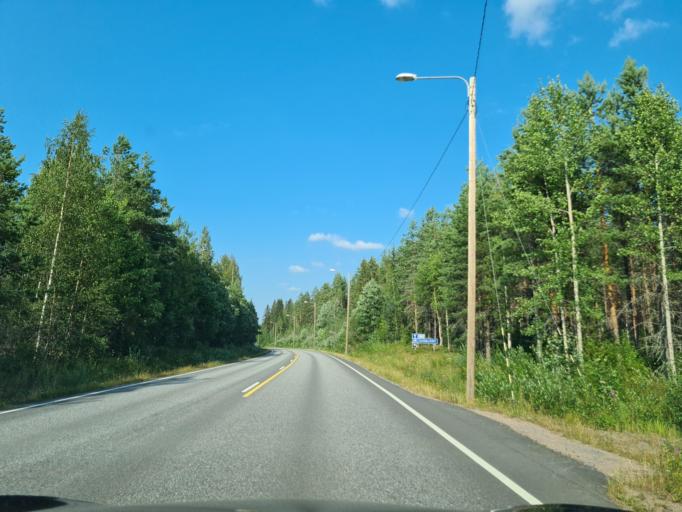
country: FI
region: Satakunta
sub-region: Pohjois-Satakunta
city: Karvia
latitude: 62.0808
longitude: 22.5205
